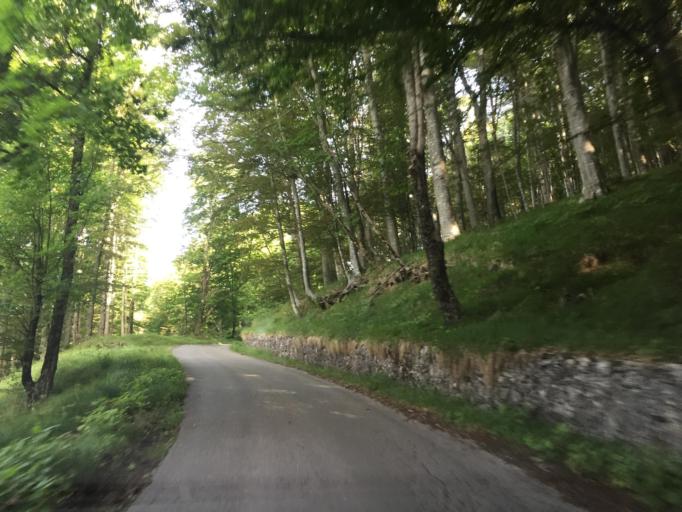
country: HR
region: Primorsko-Goranska
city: Klana
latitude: 45.4738
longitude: 14.4227
